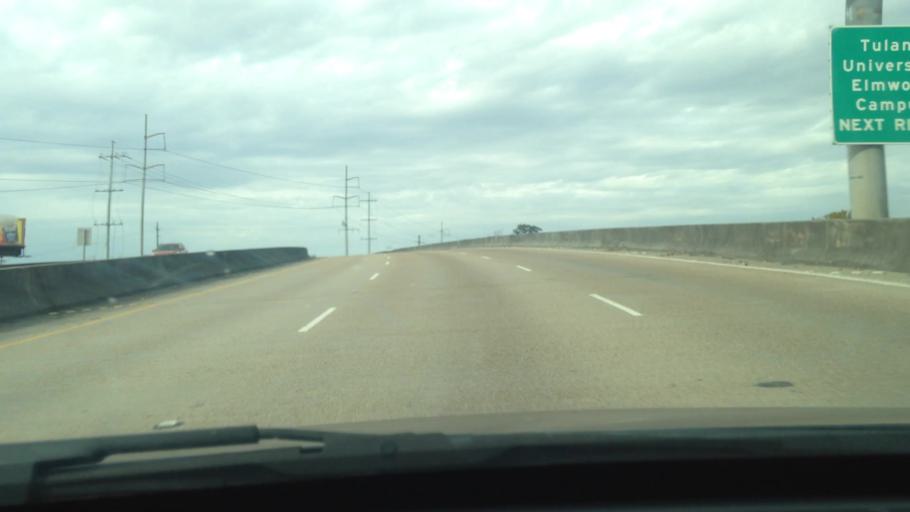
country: US
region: Louisiana
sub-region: Jefferson Parish
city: Metairie Terrace
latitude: 29.9715
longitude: -90.1714
